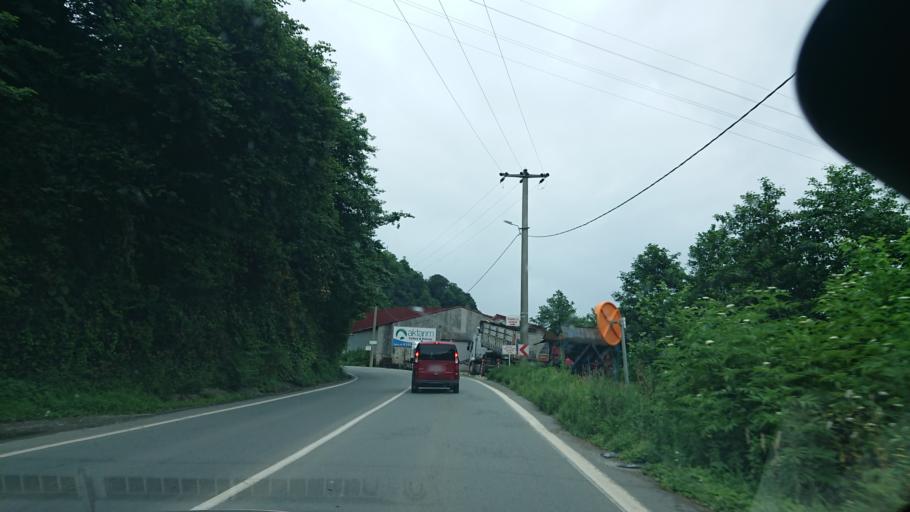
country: TR
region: Rize
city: Gundogdu
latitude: 41.0332
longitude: 40.5814
